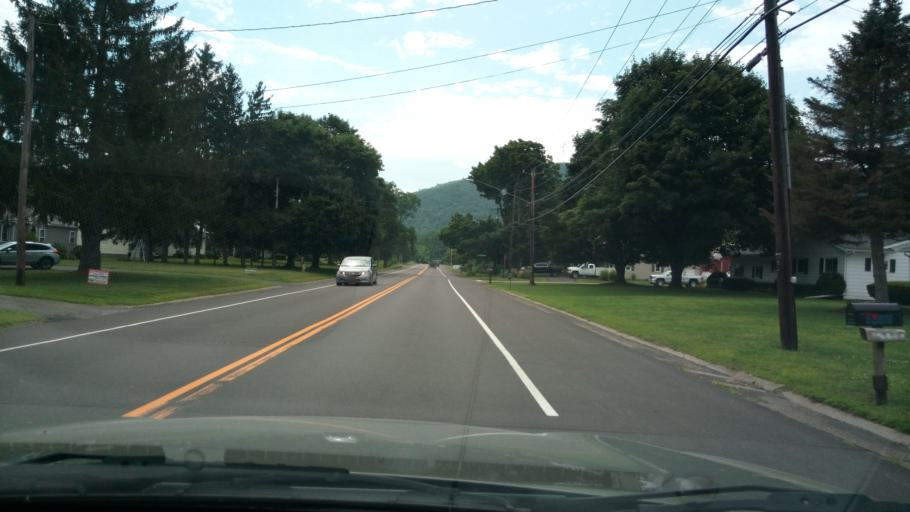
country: US
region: New York
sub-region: Chemung County
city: Southport
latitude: 42.0561
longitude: -76.7817
